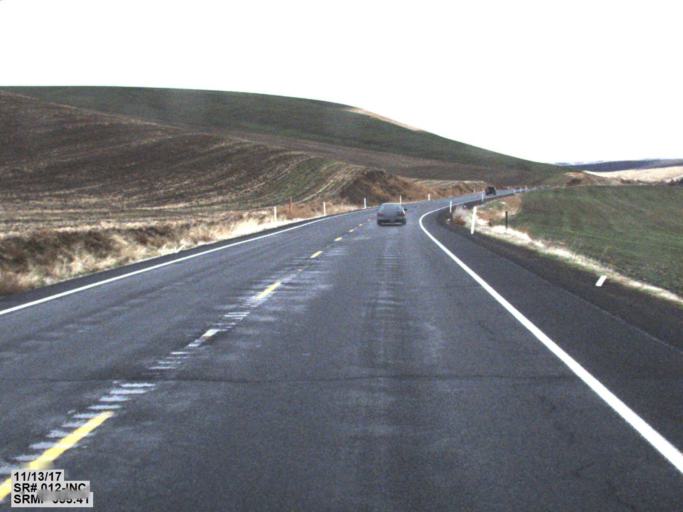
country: US
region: Washington
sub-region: Walla Walla County
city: Waitsburg
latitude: 46.2400
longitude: -118.1433
